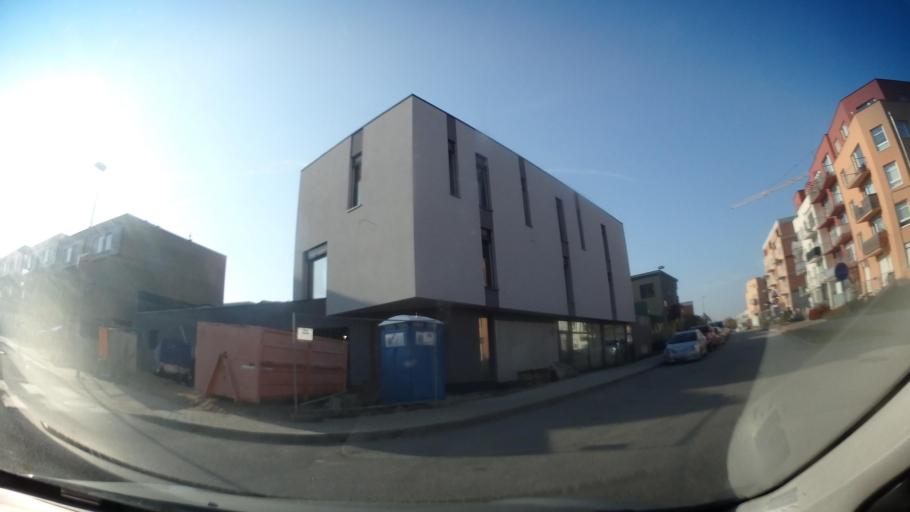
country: CZ
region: Praha
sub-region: Praha 14
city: Hostavice
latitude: 50.1021
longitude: 14.5624
